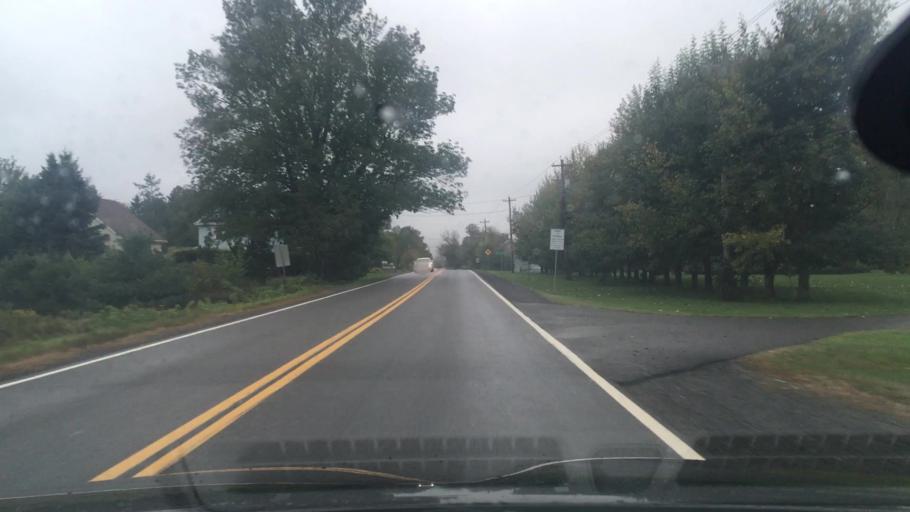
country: CA
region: Nova Scotia
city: Windsor
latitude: 44.9410
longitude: -64.1878
